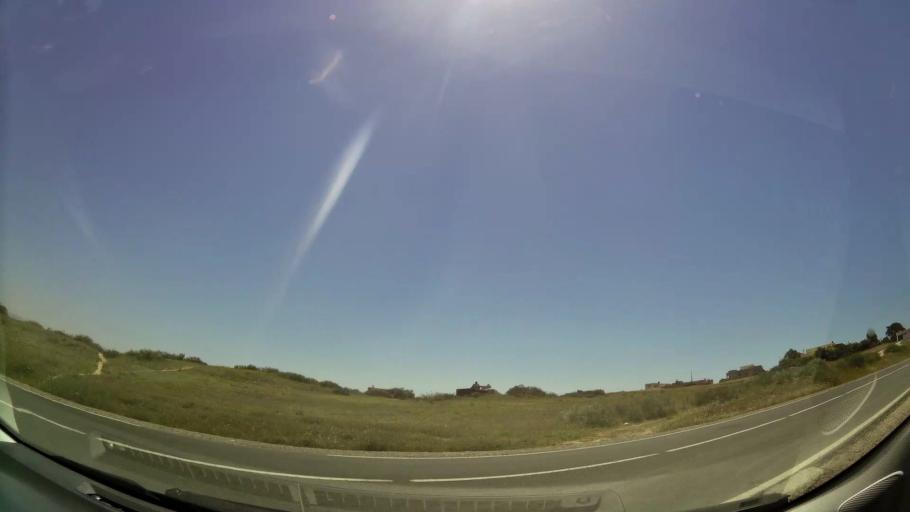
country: MA
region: Oriental
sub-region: Berkane-Taourirt
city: Madagh
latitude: 35.1221
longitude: -2.3816
